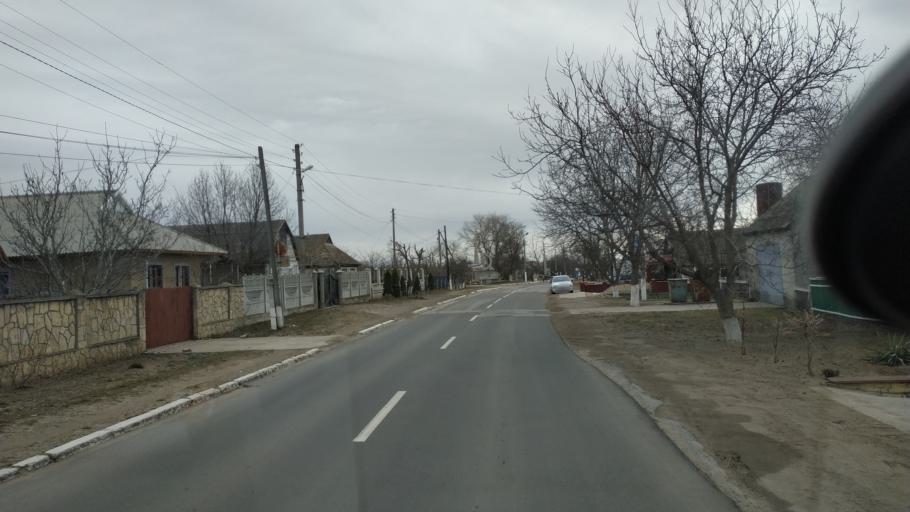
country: MD
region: Telenesti
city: Cocieri
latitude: 47.2972
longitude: 29.1163
